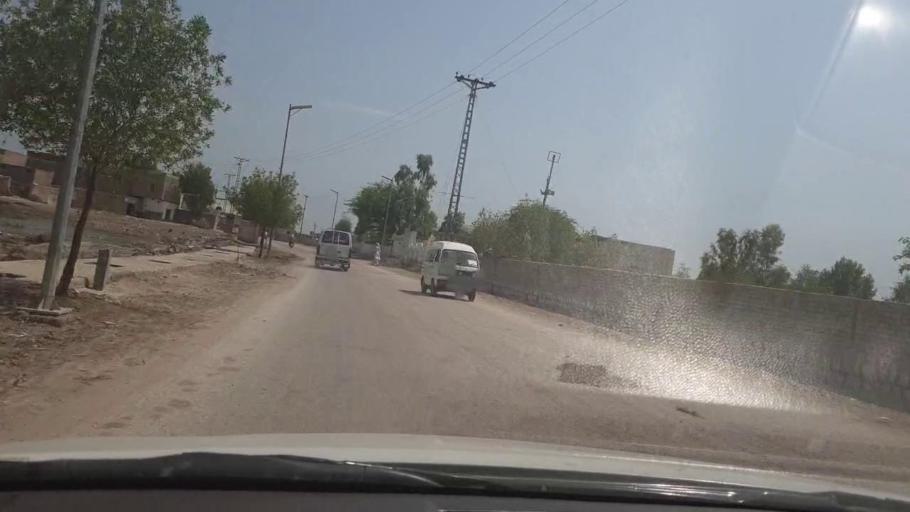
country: PK
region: Sindh
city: Garhi Yasin
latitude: 27.9061
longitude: 68.5066
